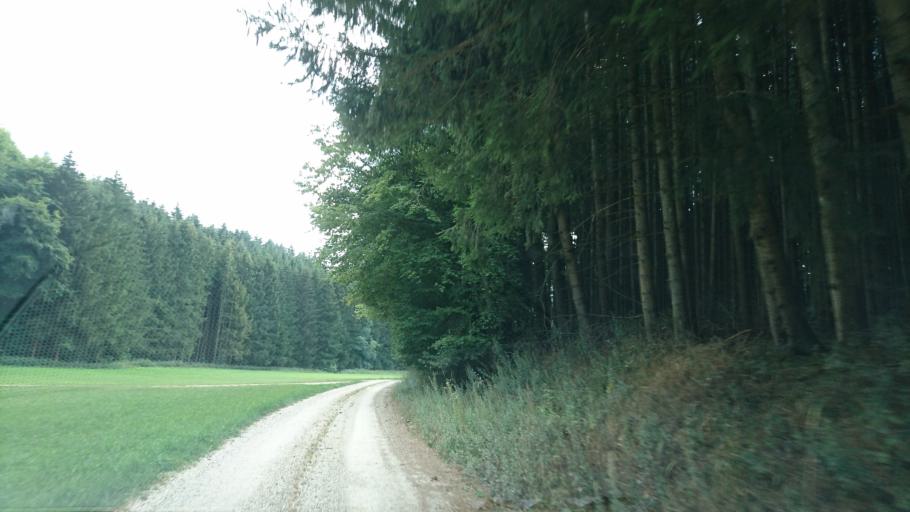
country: DE
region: Bavaria
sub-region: Swabia
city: Zusmarshausen
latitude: 48.4247
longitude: 10.6134
